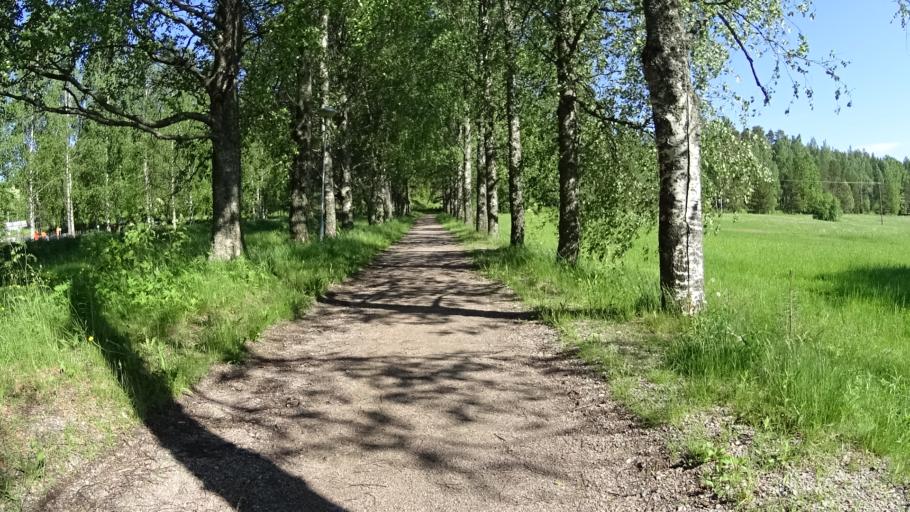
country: FI
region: Uusimaa
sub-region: Helsinki
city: Kauniainen
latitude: 60.3177
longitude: 24.6913
